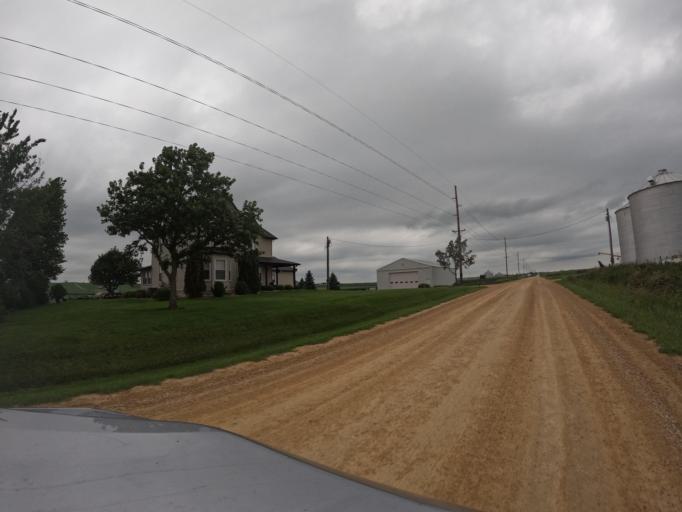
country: US
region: Iowa
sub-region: Clinton County
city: De Witt
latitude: 41.9410
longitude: -90.5870
